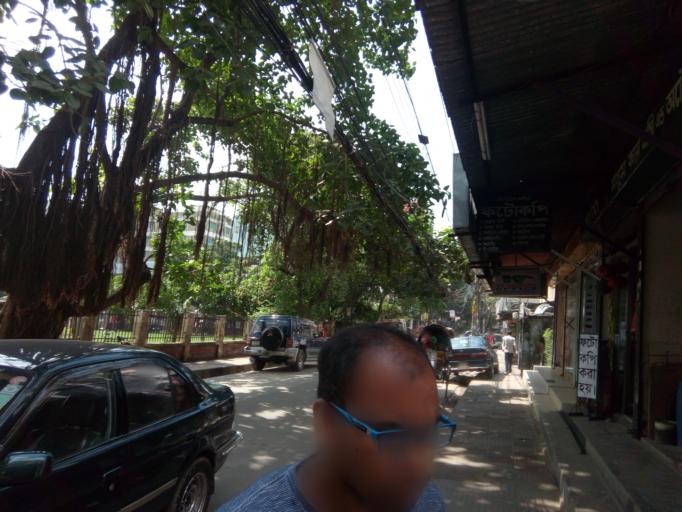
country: BD
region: Dhaka
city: Azimpur
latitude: 23.7635
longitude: 90.3643
